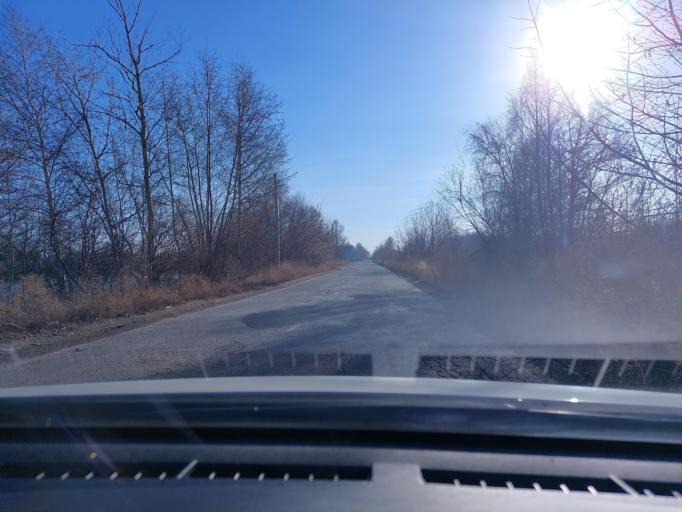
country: RU
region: Irkutsk
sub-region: Irkutskiy Rayon
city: Irkutsk
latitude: 52.3122
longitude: 104.2695
